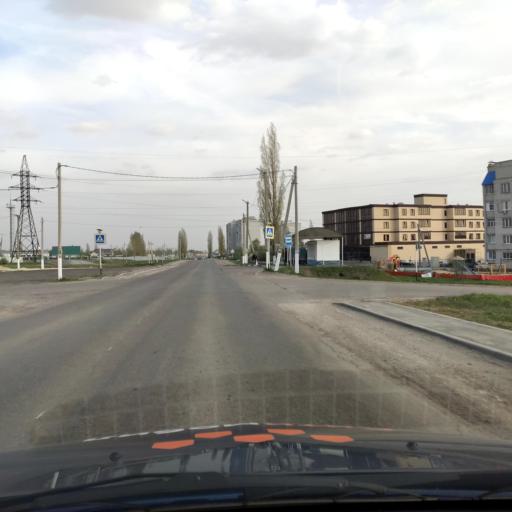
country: RU
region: Voronezj
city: Novaya Usman'
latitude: 51.6573
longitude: 39.4048
